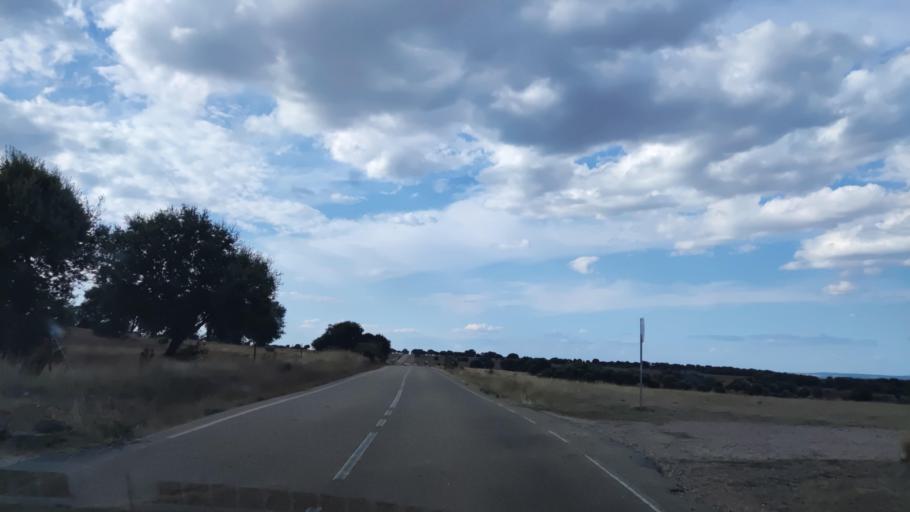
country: ES
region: Castille and Leon
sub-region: Provincia de Salamanca
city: Martiago
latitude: 40.4774
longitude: -6.4906
